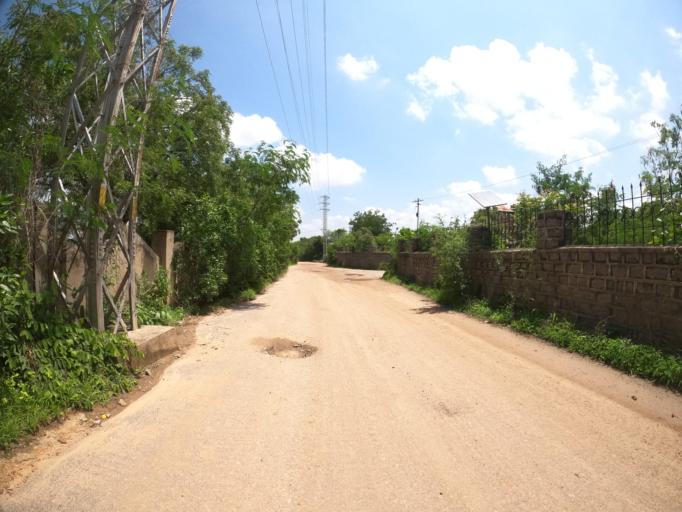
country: IN
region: Telangana
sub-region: Medak
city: Serilingampalle
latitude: 17.3727
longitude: 78.3248
